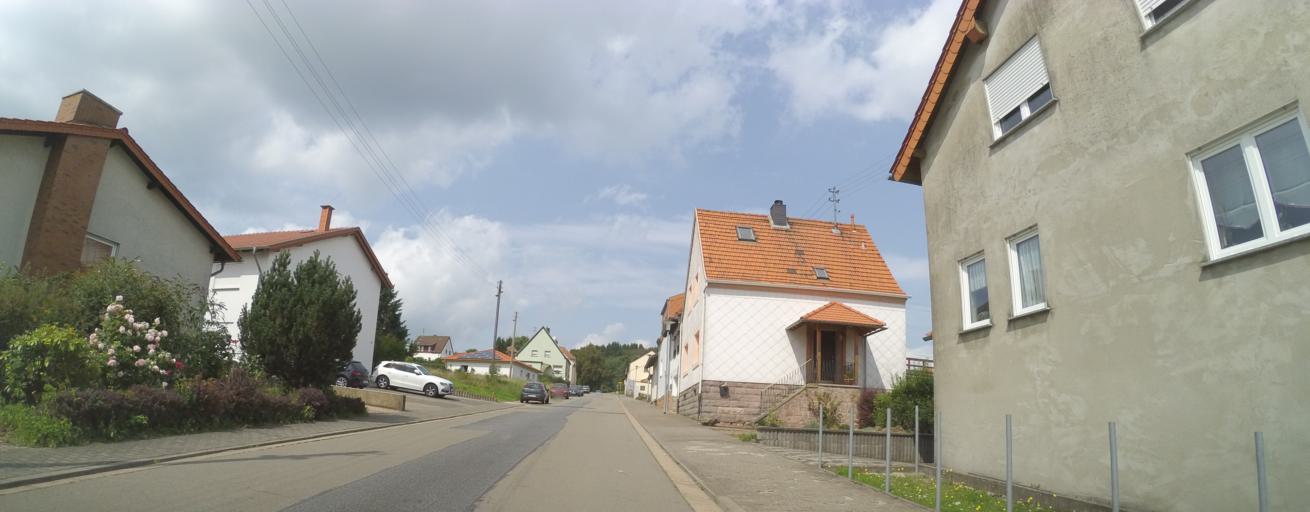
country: DE
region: Rheinland-Pfalz
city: Breitenbach
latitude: 49.3894
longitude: 7.2662
